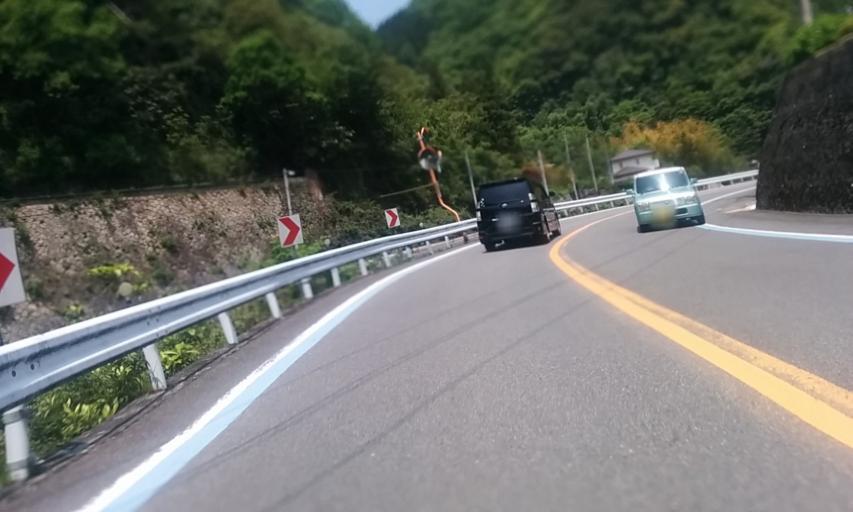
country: JP
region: Ehime
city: Niihama
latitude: 33.9159
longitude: 133.3119
